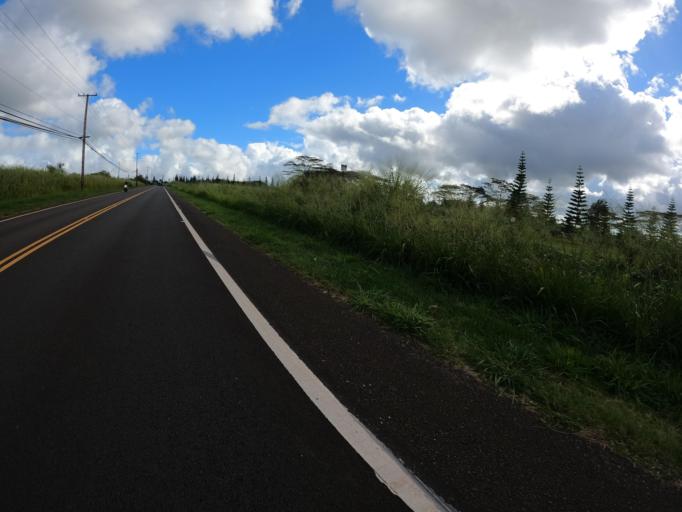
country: US
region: Hawaii
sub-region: Honolulu County
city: Whitmore Village
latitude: 21.5136
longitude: -158.0125
